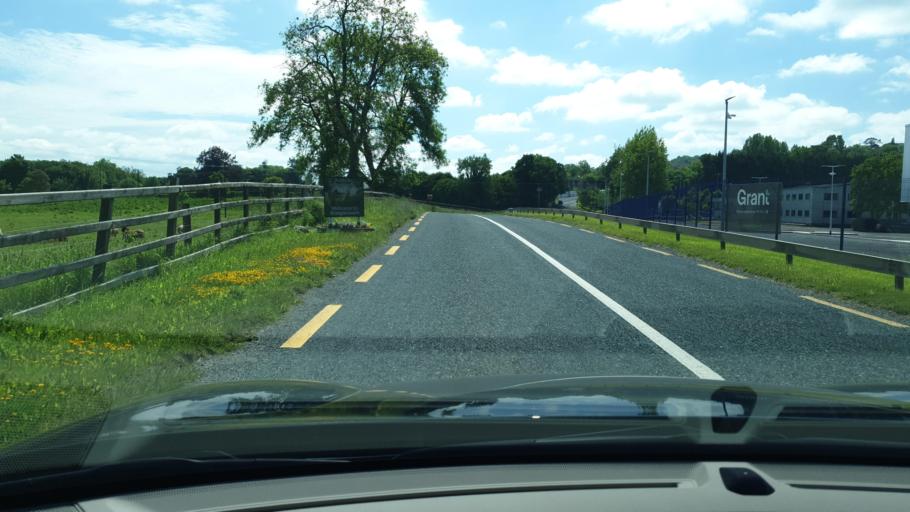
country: IE
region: Ulster
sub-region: An Cabhan
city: Kingscourt
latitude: 53.9063
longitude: -6.7880
